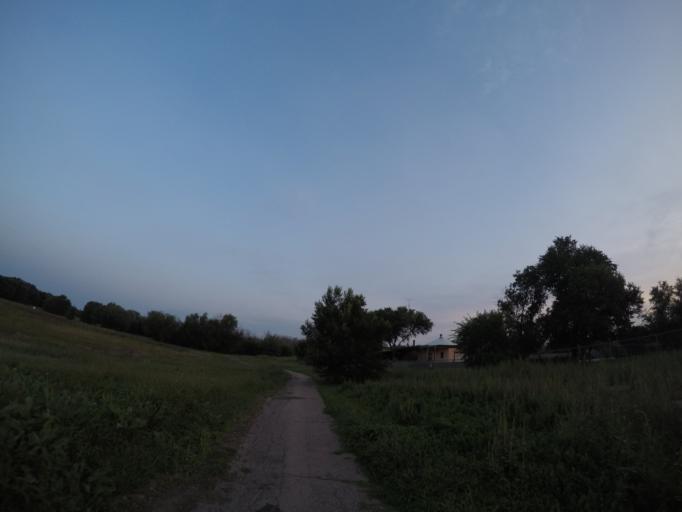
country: US
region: New Mexico
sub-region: Curry County
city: Clovis
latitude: 34.4290
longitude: -103.1886
